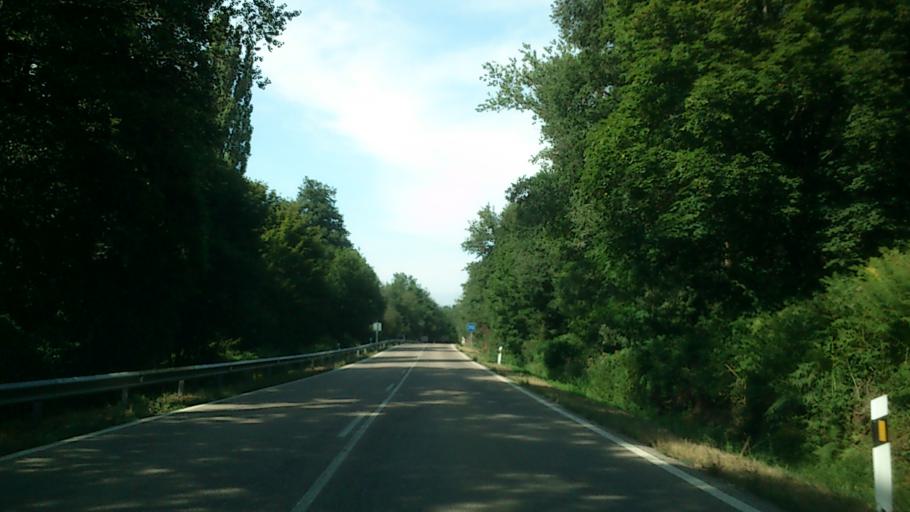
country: ES
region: Castille and Leon
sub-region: Provincia de Burgos
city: Medina de Pomar
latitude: 43.0170
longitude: -3.4834
